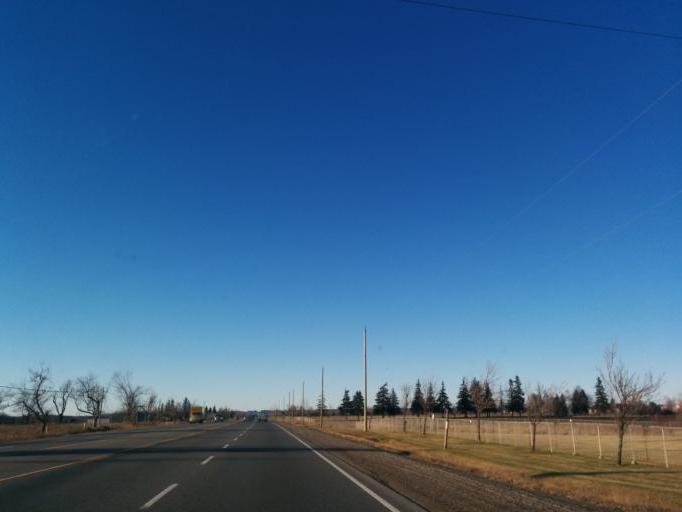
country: CA
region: Ontario
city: Brampton
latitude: 43.7775
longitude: -79.8836
